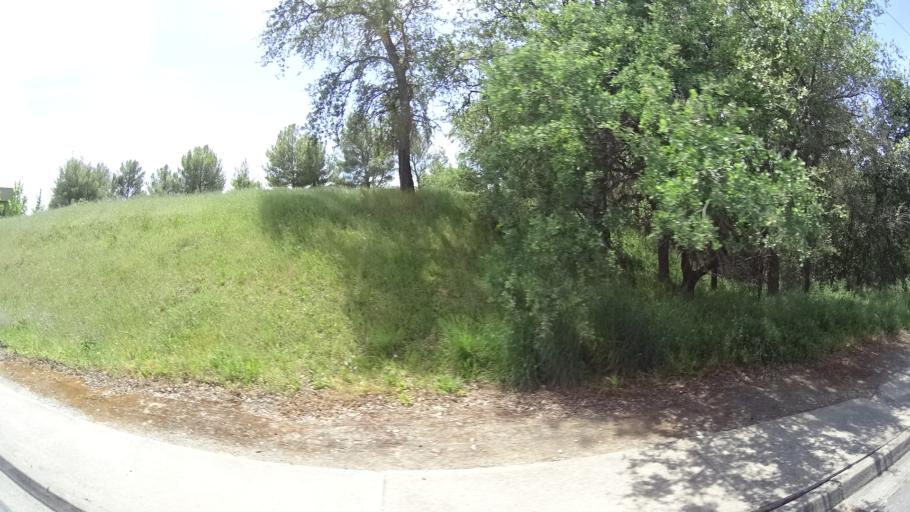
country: US
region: California
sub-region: Placer County
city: Rocklin
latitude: 38.7857
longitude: -121.2500
